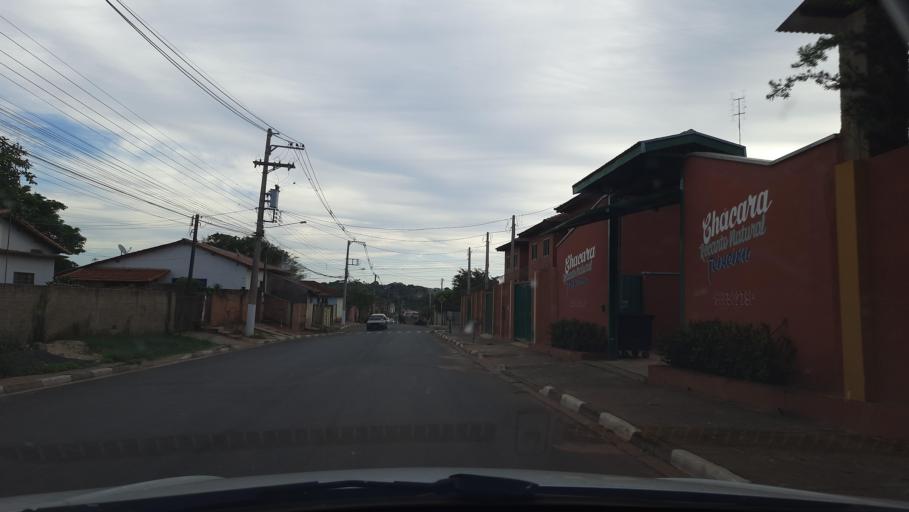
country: BR
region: Sao Paulo
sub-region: Casa Branca
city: Casa Branca
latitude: -21.7650
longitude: -47.0863
